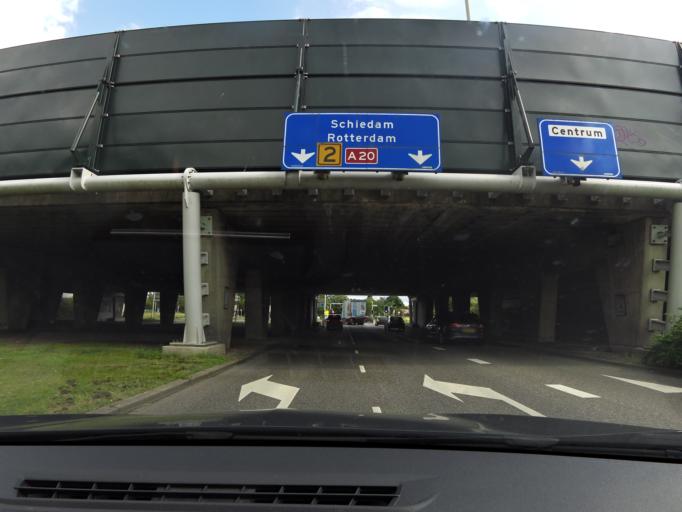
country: NL
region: South Holland
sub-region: Gemeente Vlaardingen
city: Vlaardingen
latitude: 51.9223
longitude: 4.3472
